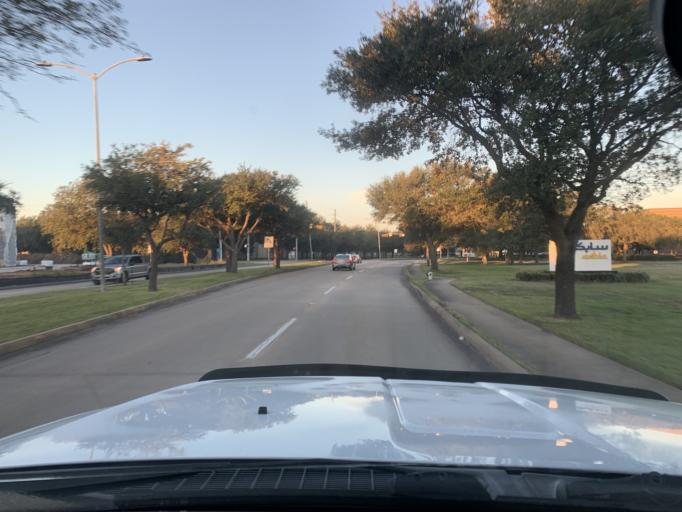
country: US
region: Texas
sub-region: Fort Bend County
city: Meadows Place
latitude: 29.6458
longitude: -95.6067
